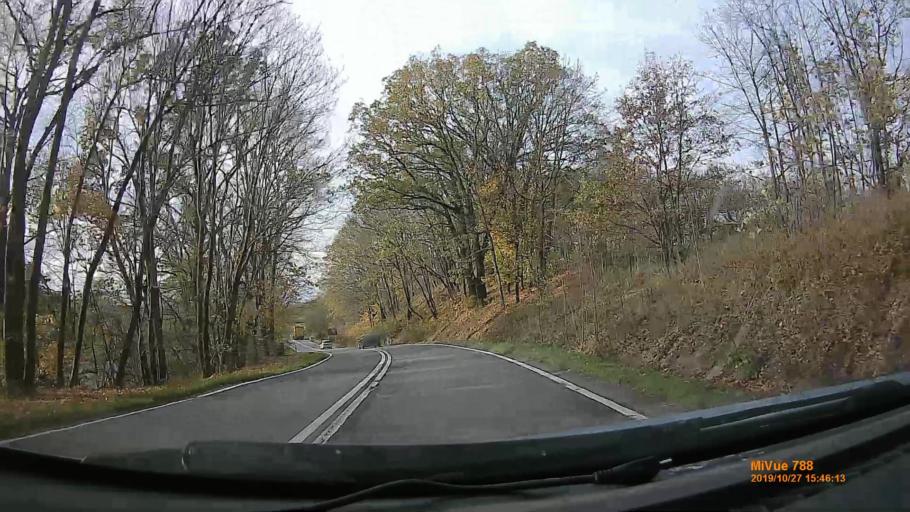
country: PL
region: Lower Silesian Voivodeship
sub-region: Powiat klodzki
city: Bozkow
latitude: 50.4804
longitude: 16.5873
